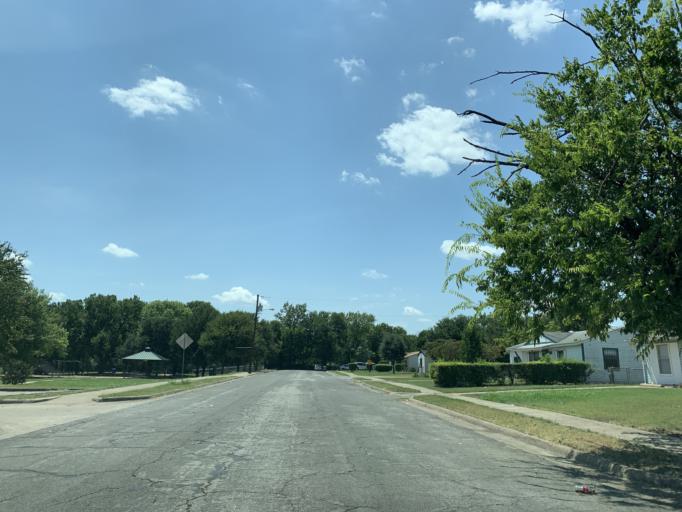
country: US
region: Texas
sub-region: Dallas County
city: Hutchins
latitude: 32.6821
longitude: -96.7814
